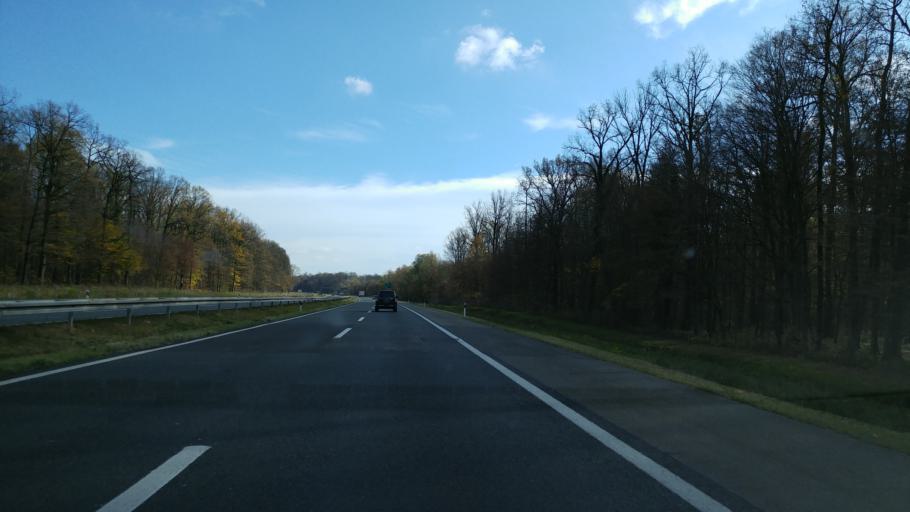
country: HR
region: Sisacko-Moslavacka
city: Novska
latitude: 45.3386
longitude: 16.9242
